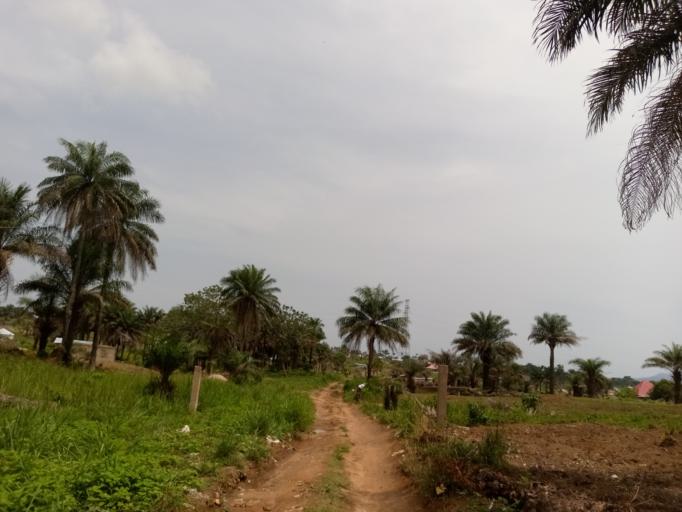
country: SL
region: Western Area
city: Waterloo
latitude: 8.3317
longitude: -13.0220
